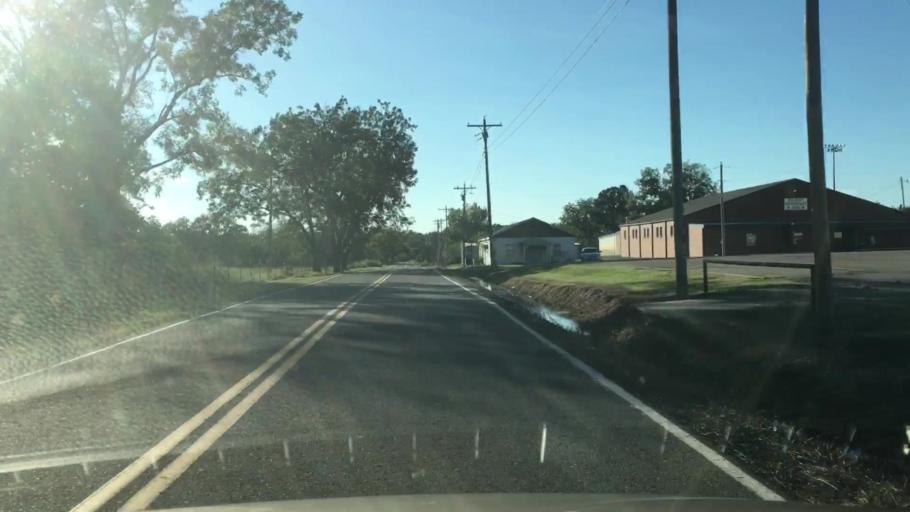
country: US
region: Oklahoma
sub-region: Muskogee County
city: Fort Gibson
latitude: 35.9297
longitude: -95.1443
